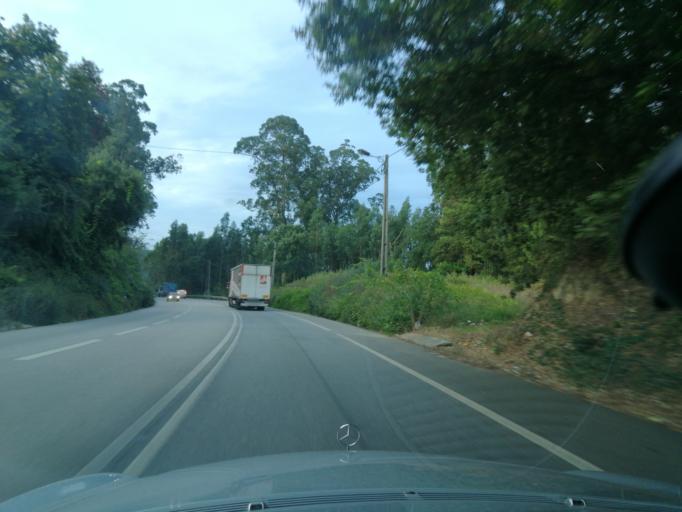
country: PT
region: Aveiro
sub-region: Agueda
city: Valongo
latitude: 40.6243
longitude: -8.4613
